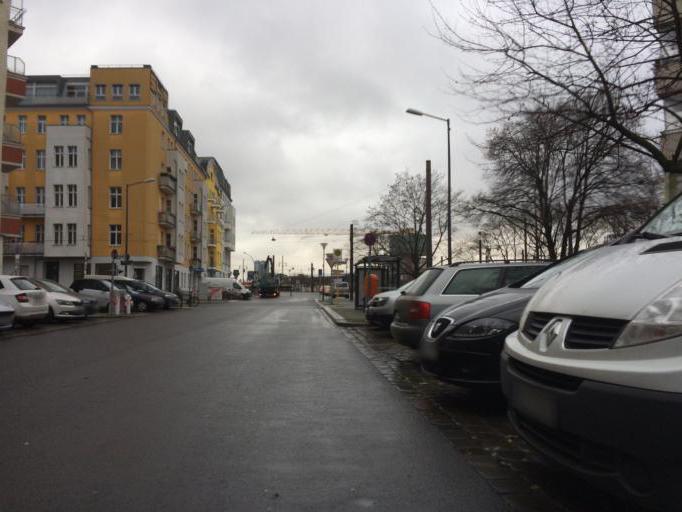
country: DE
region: Berlin
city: Friedrichshain Bezirk
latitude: 52.5087
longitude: 13.4487
